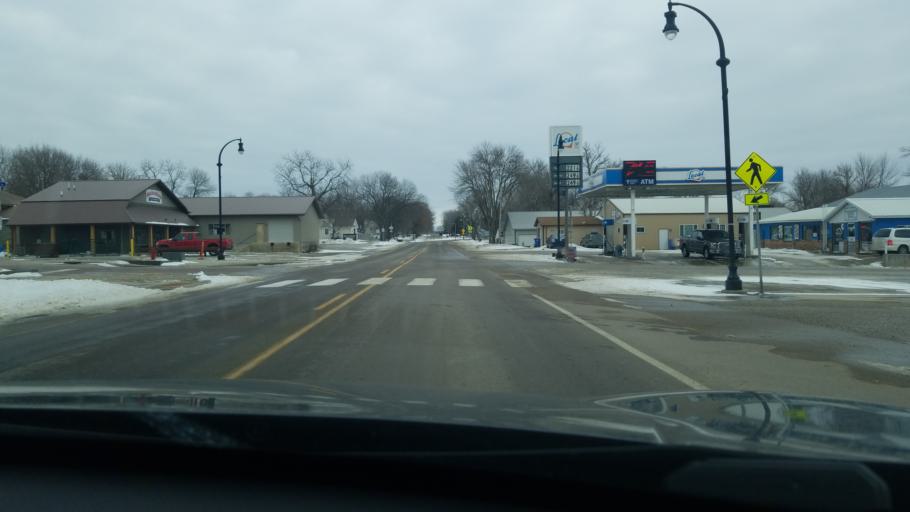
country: US
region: South Dakota
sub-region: Minnehaha County
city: Brandon
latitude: 43.4530
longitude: -96.4347
